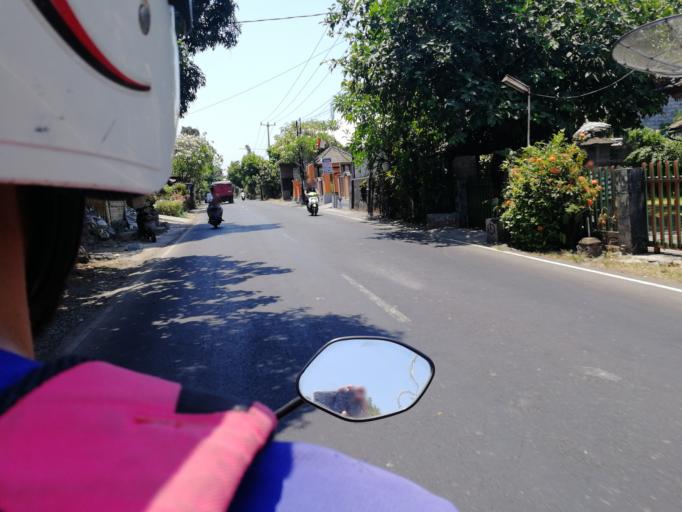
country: ID
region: Bali
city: Banjar Trunyan
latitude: -8.1431
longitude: 115.3942
